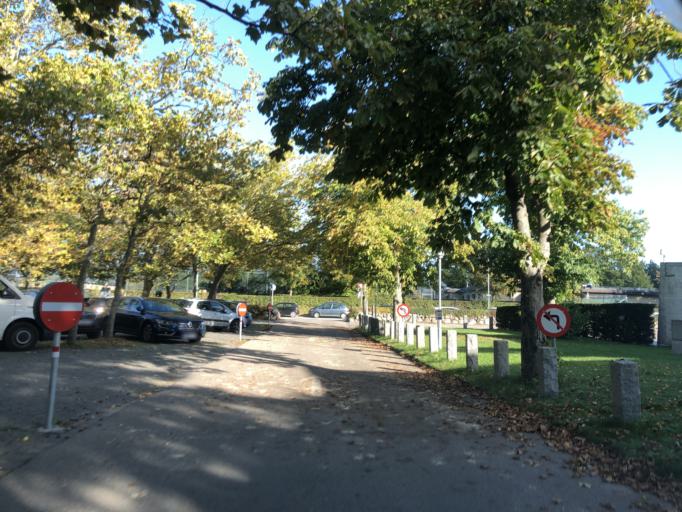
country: DK
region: Capital Region
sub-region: Glostrup Kommune
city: Glostrup
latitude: 55.6713
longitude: 12.3886
